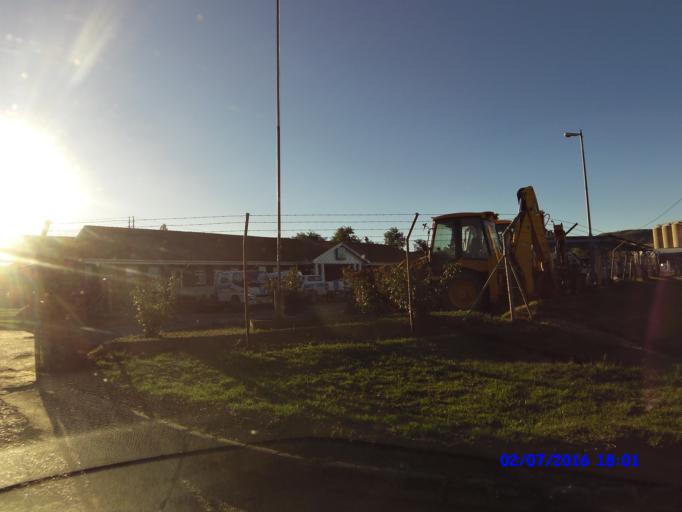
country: LS
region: Maseru
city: Maseru
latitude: -29.2995
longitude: 27.4823
